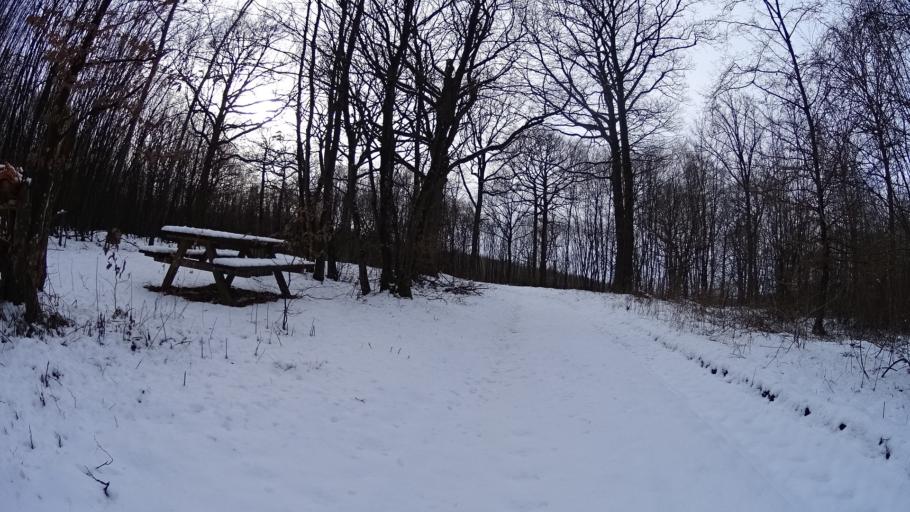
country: AT
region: Lower Austria
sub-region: Politischer Bezirk Korneuburg
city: Leobendorf
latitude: 48.4149
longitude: 16.3317
